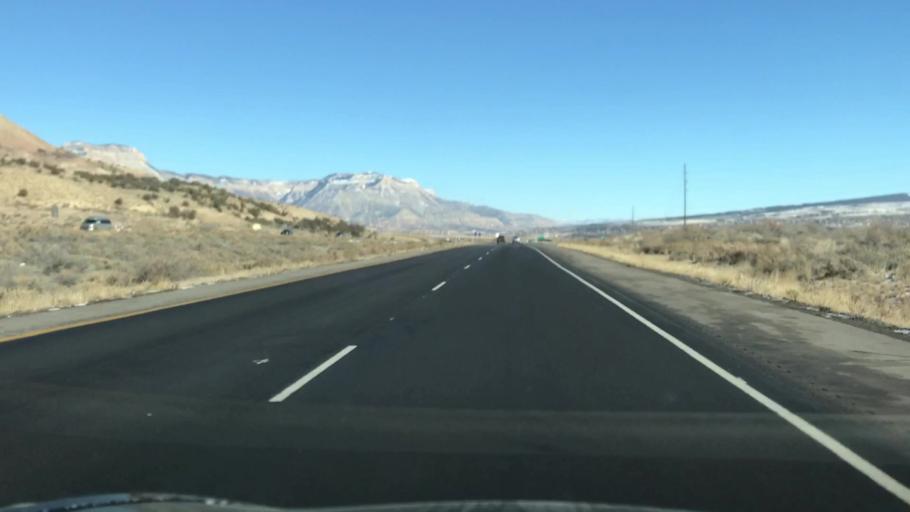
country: US
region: Colorado
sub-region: Garfield County
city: Parachute
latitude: 39.4204
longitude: -108.0866
